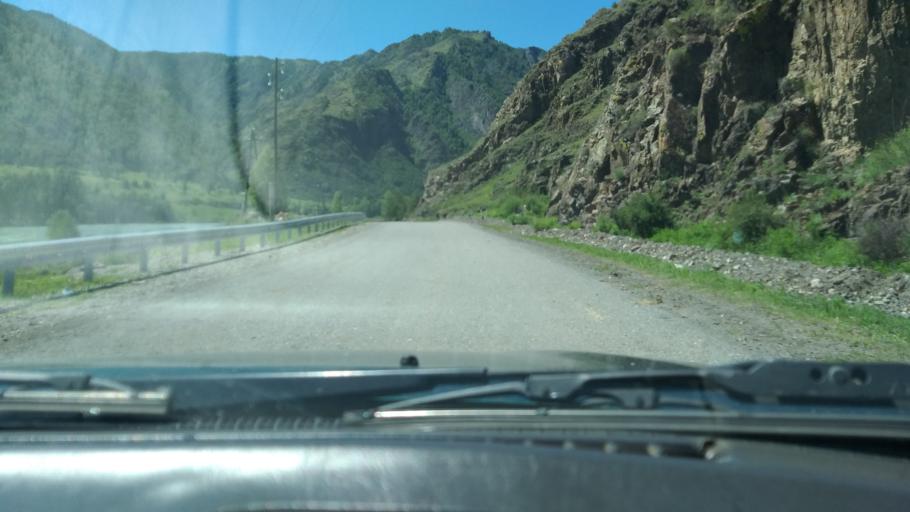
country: RU
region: Altay
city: Chemal
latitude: 51.2326
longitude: 86.0799
